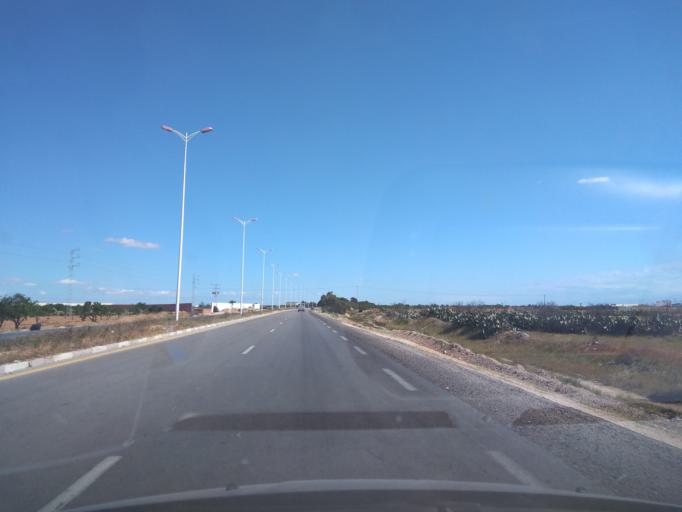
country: TN
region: Safaqis
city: Al Qarmadah
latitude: 34.8391
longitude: 10.7363
